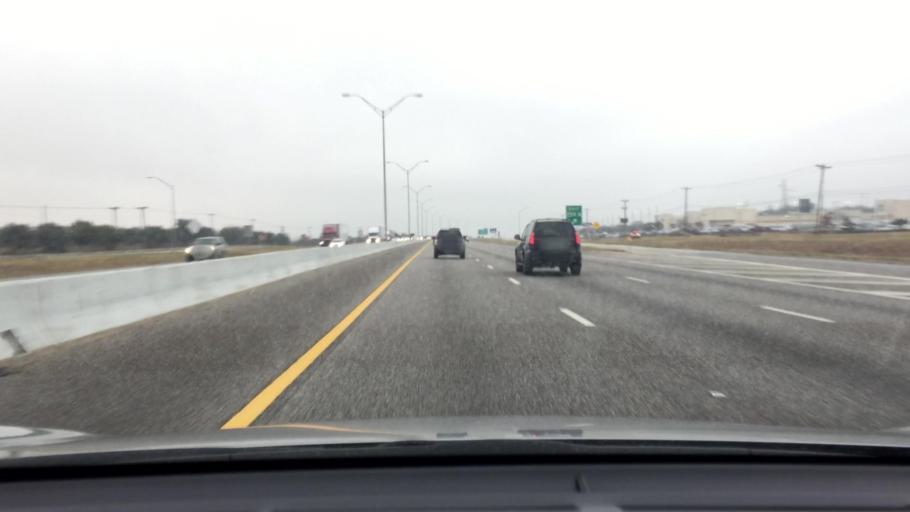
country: US
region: Texas
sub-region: Williamson County
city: Georgetown
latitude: 30.5791
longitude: -97.6928
